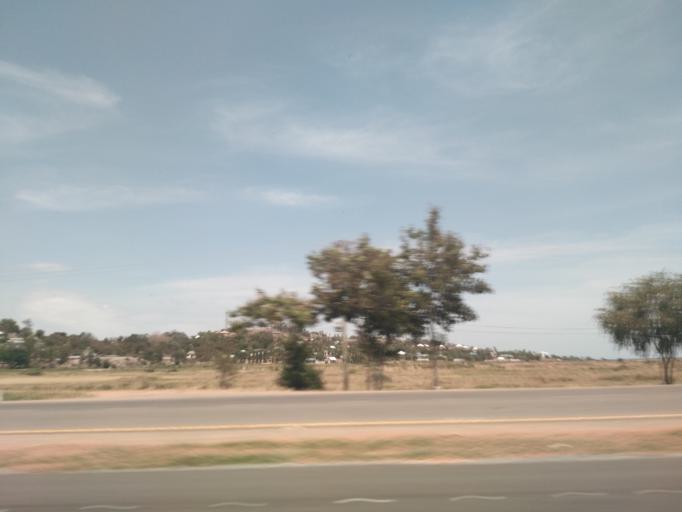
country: TZ
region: Mwanza
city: Mwanza
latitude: -2.4510
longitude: 32.9207
